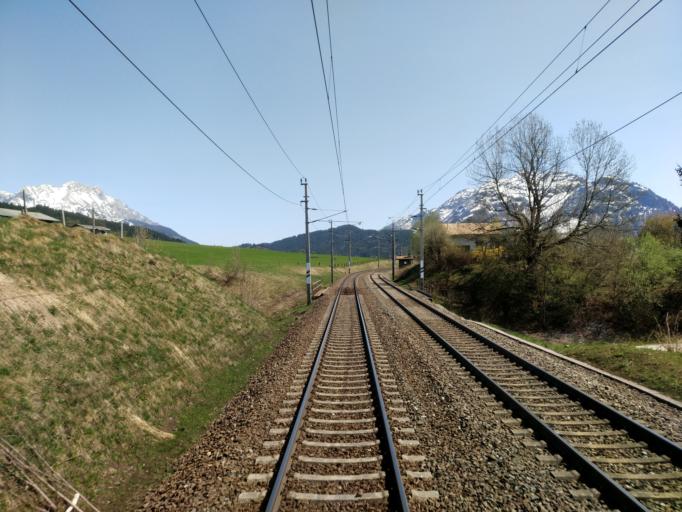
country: AT
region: Tyrol
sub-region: Politischer Bezirk Kitzbuhel
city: Fieberbrunn
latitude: 47.4707
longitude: 12.5671
